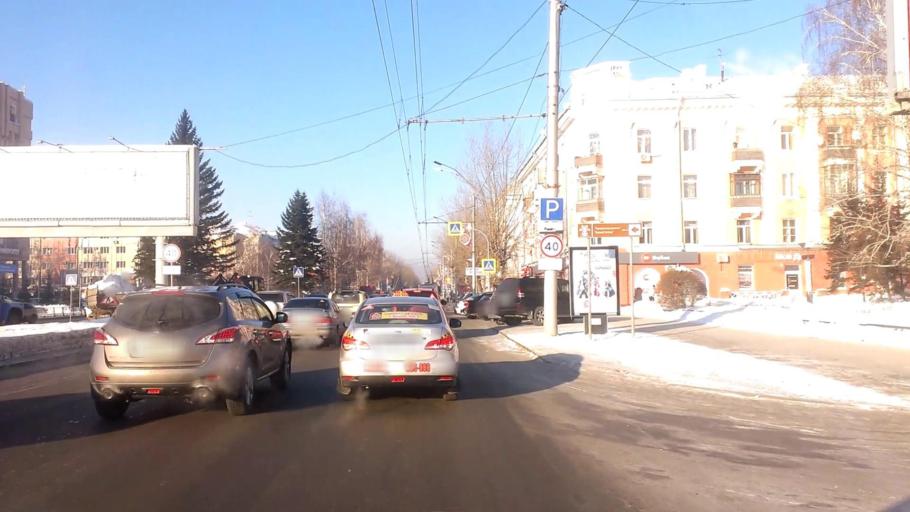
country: RU
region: Altai Krai
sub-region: Gorod Barnaulskiy
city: Barnaul
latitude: 53.3475
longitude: 83.7779
